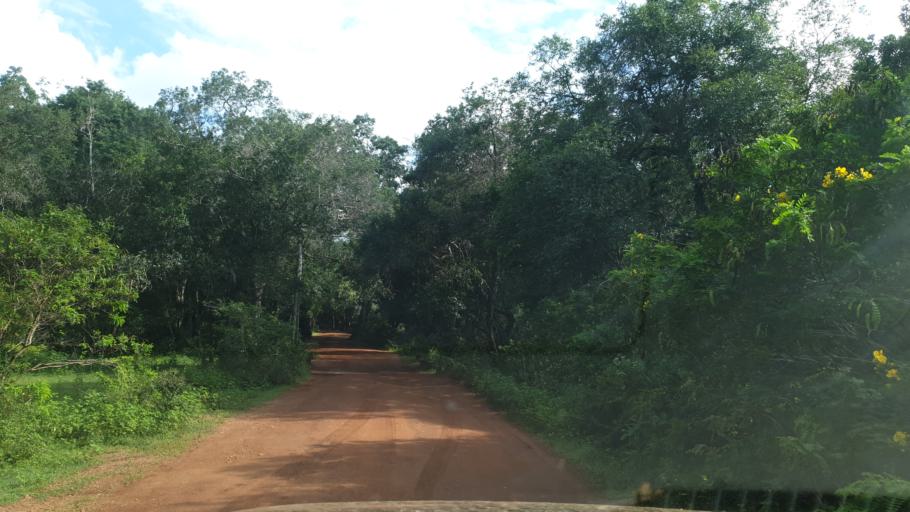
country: LK
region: North Central
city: Anuradhapura
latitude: 8.3782
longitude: 80.0696
